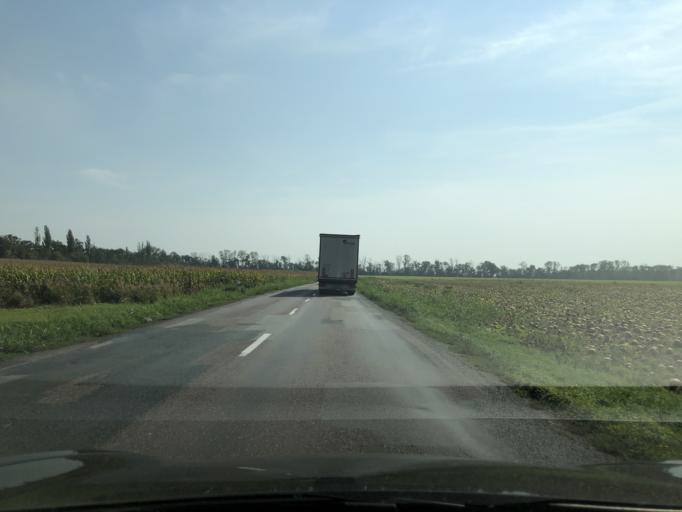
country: CZ
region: South Moravian
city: Brezi
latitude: 48.8255
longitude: 16.5399
